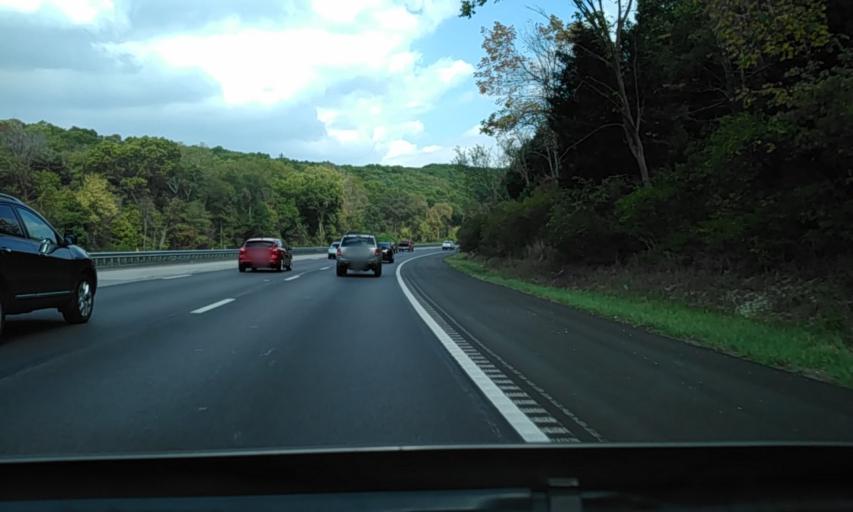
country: US
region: Missouri
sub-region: Saint Louis County
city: Valley Park
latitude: 38.5238
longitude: -90.5445
